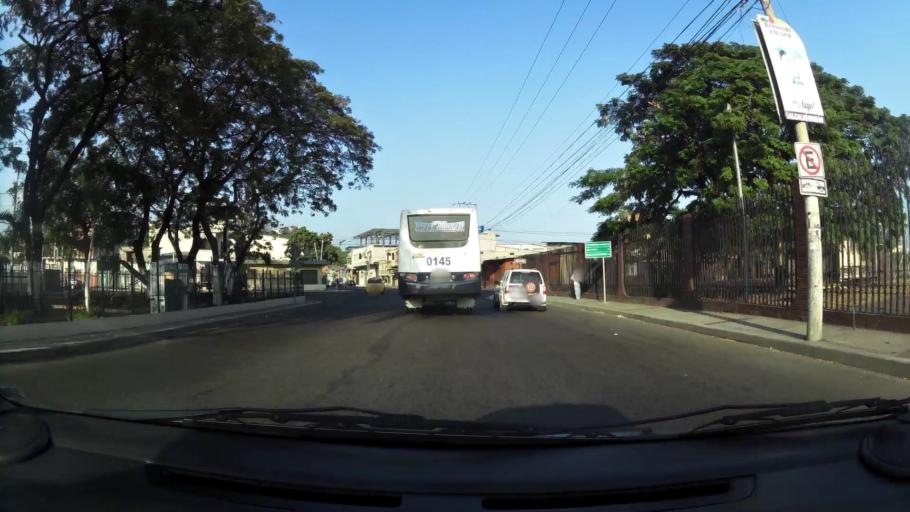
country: EC
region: Guayas
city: Eloy Alfaro
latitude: -2.1670
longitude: -79.8475
